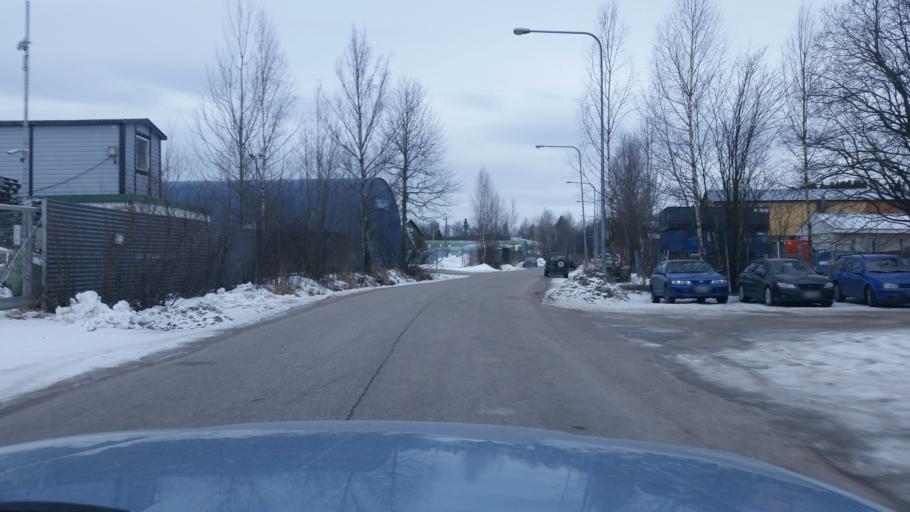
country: FI
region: Uusimaa
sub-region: Helsinki
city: Vantaa
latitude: 60.2562
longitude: 25.0571
